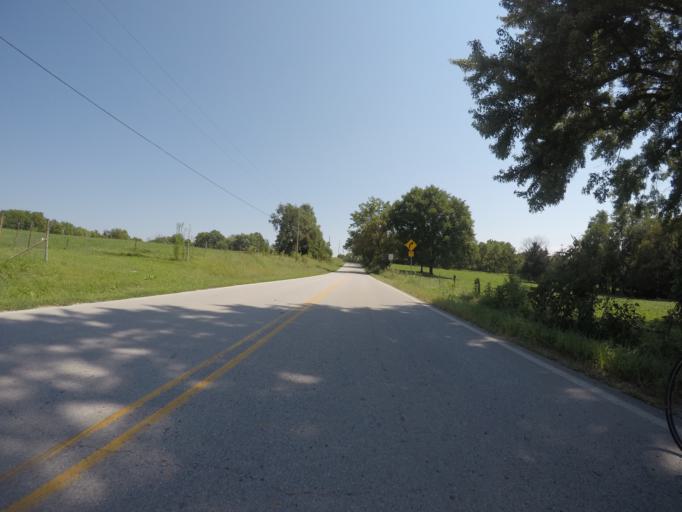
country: US
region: Kansas
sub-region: Leavenworth County
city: Lansing
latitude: 39.2462
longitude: -94.8736
